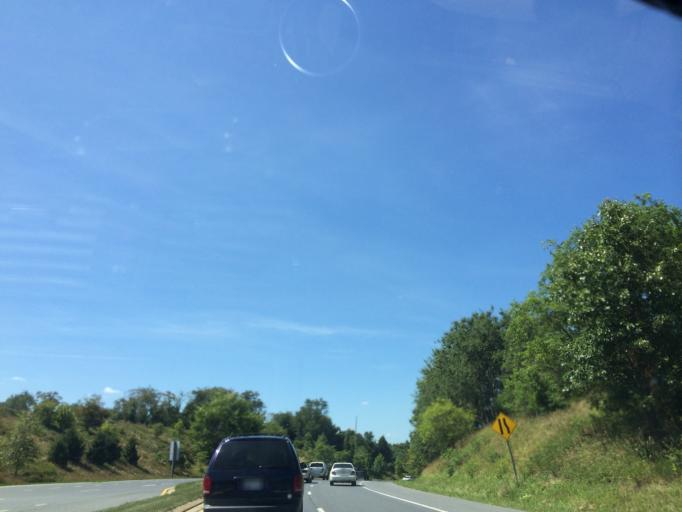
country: US
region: Maryland
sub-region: Carroll County
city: Sykesville
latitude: 39.3772
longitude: -76.9675
